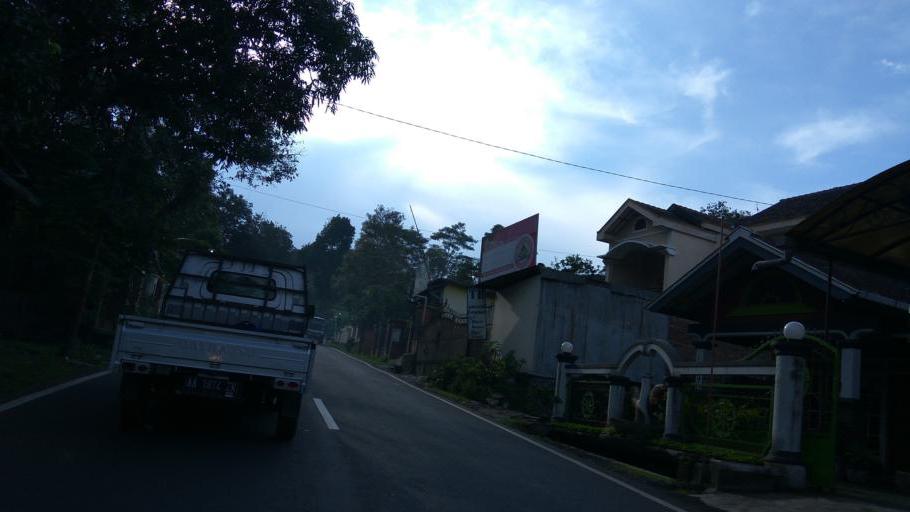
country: ID
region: Central Java
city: Salatiga
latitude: -7.3672
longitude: 110.4623
